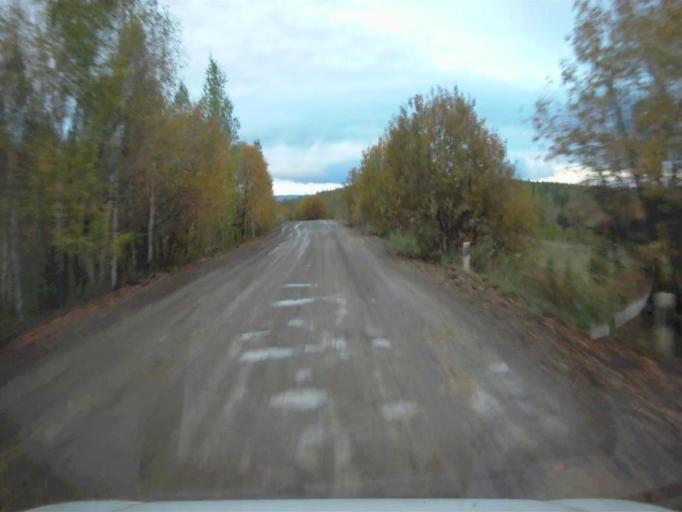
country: RU
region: Sverdlovsk
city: Mikhaylovsk
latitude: 56.2083
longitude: 59.2084
